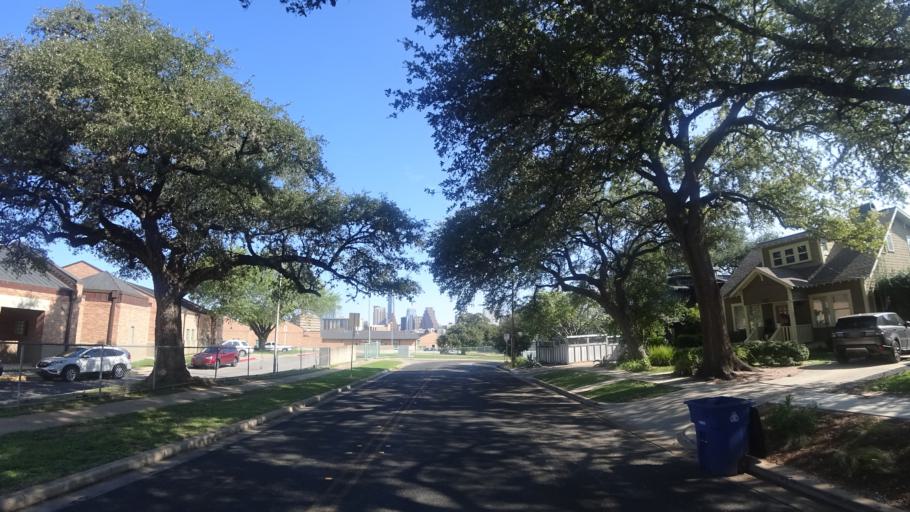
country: US
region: Texas
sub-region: Travis County
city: Austin
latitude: 30.2523
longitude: -97.7501
